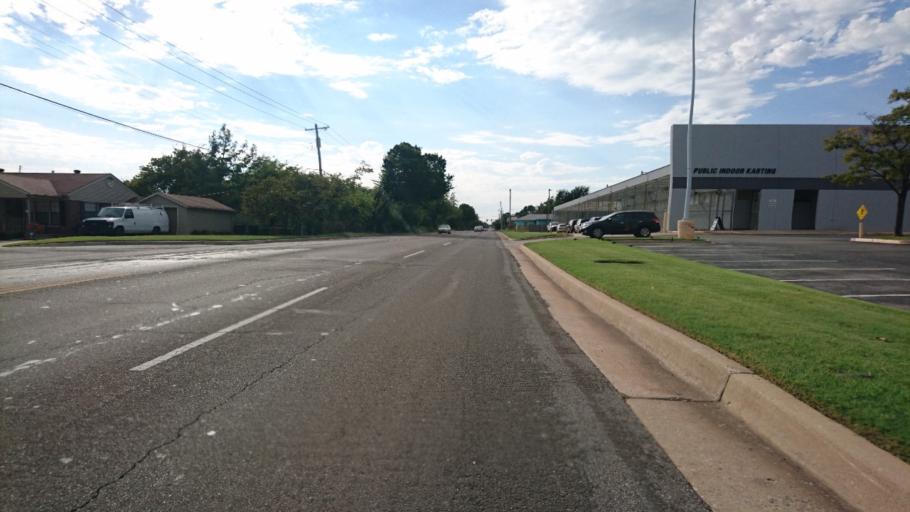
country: US
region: Oklahoma
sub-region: Oklahoma County
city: Nichols Hills
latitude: 35.5077
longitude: -97.5669
